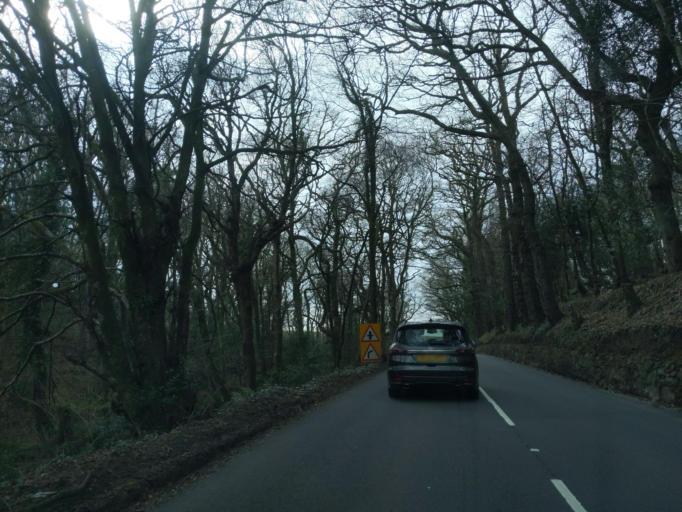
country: GB
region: England
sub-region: Devon
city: Okehampton
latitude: 50.6970
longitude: -3.8429
